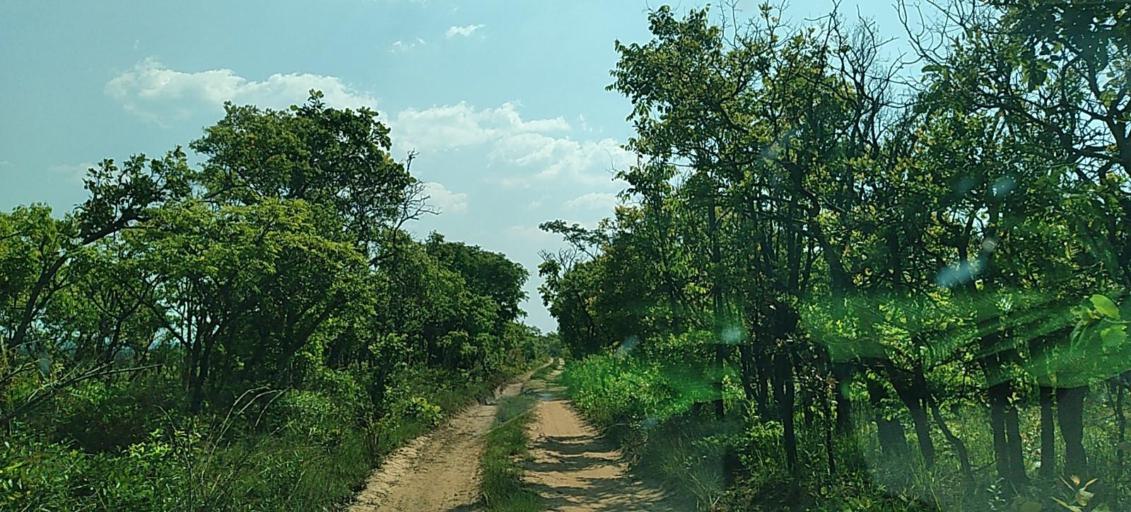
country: CD
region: Katanga
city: Kolwezi
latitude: -11.2697
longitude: 24.9931
